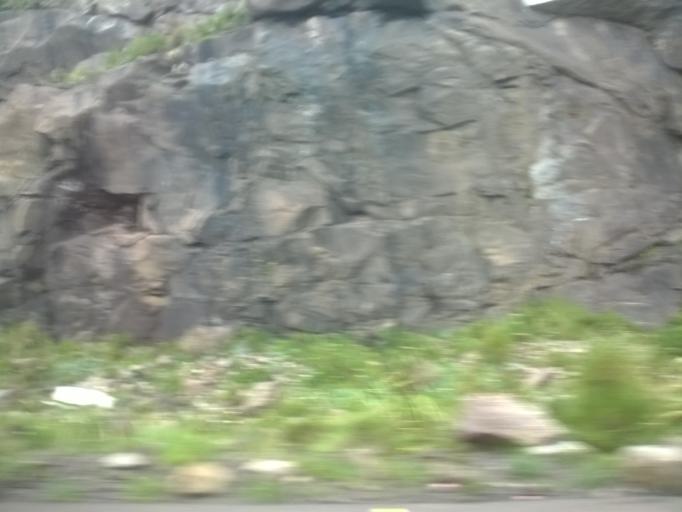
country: LS
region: Butha-Buthe
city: Butha-Buthe
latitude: -29.0691
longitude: 28.3800
